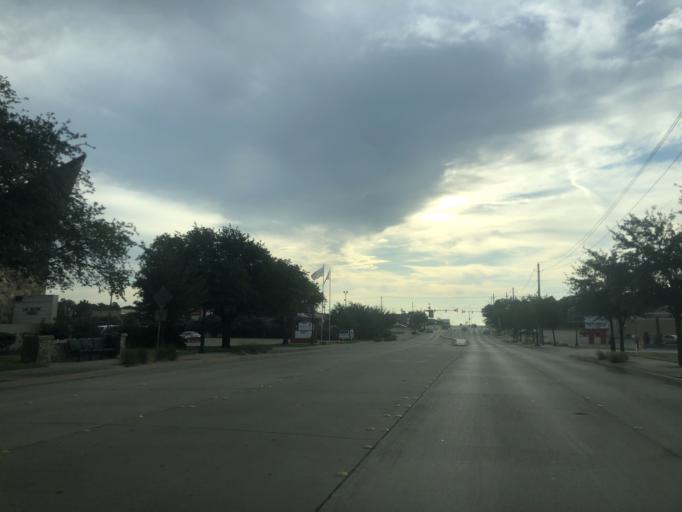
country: US
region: Texas
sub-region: Tarrant County
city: Hurst
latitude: 32.8236
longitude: -97.1888
